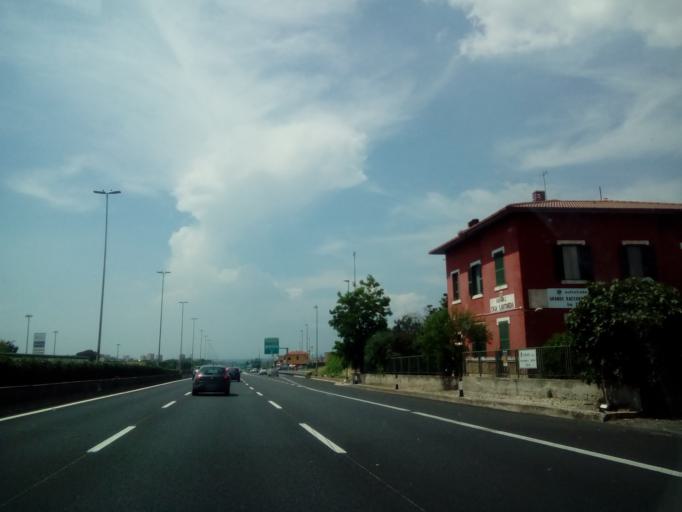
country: IT
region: Latium
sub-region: Citta metropolitana di Roma Capitale
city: Colle Verde
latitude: 41.9725
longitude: 12.5498
